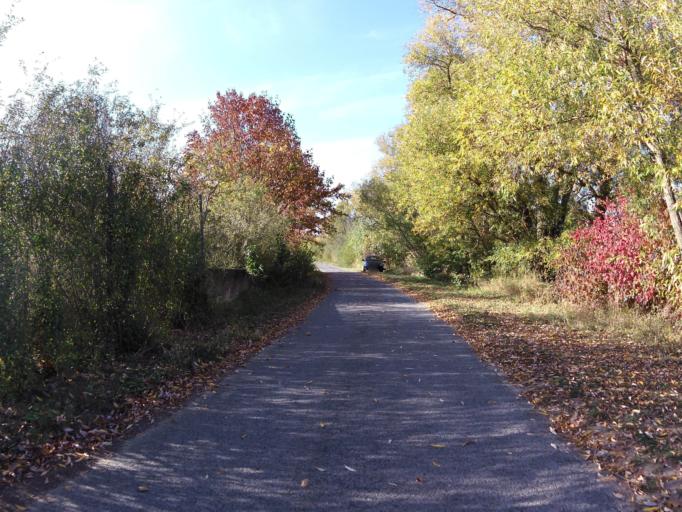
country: DE
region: Bavaria
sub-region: Regierungsbezirk Unterfranken
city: Eibelstadt
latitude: 49.7163
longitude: 10.0087
